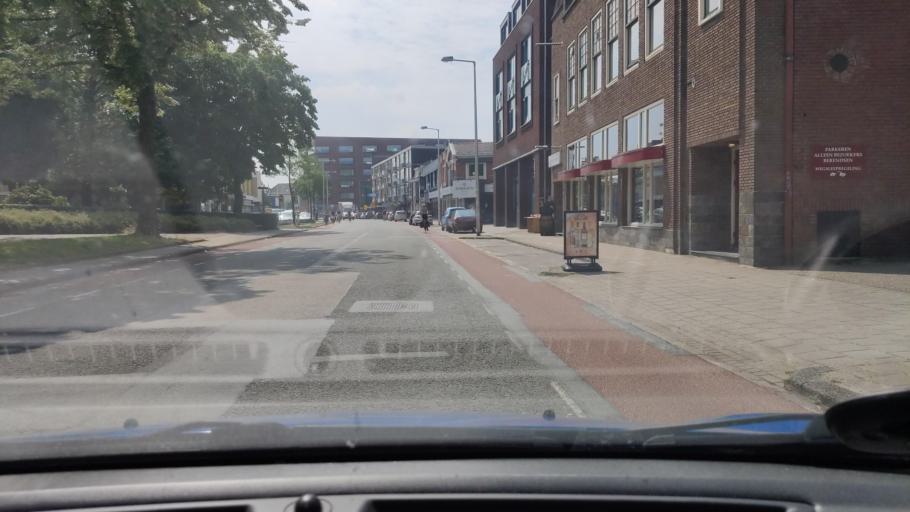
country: NL
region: Overijssel
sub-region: Gemeente Enschede
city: Enschede
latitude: 52.2250
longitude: 6.8915
